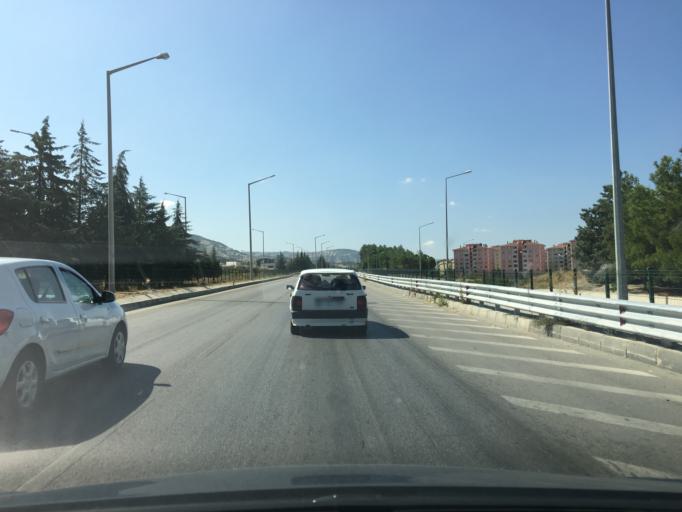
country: TR
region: Burdur
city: Burdur
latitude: 37.7386
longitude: 30.3117
